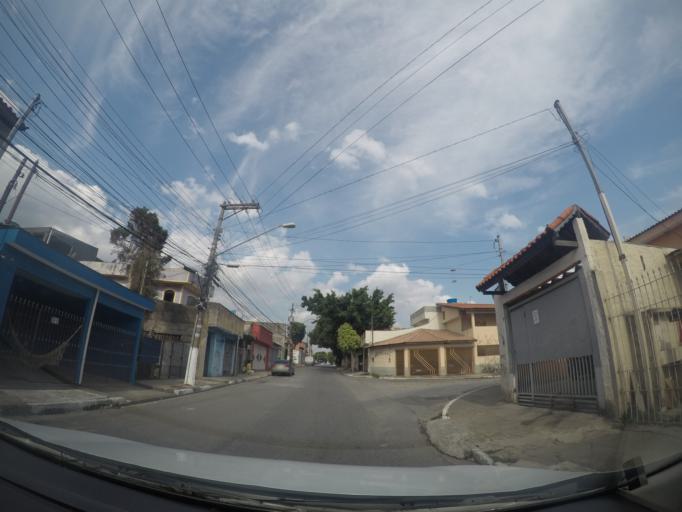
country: BR
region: Sao Paulo
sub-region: Guarulhos
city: Guarulhos
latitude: -23.4531
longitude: -46.5054
